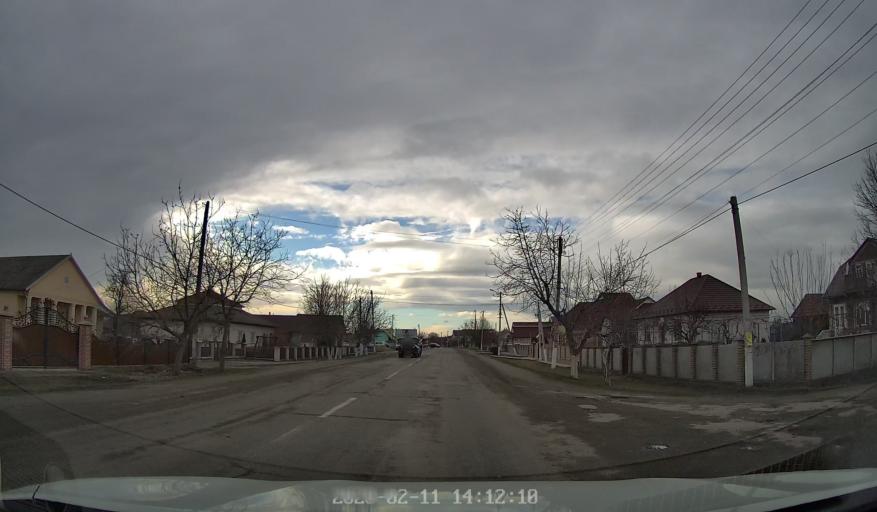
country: RO
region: Botosani
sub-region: Comuna Darabani
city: Bajura
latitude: 48.2233
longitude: 26.4945
